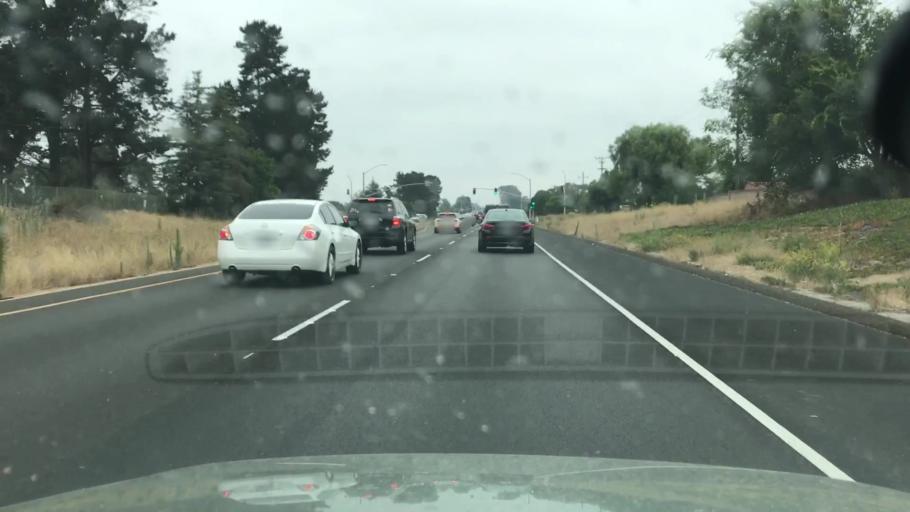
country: US
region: California
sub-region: Santa Barbara County
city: Orcutt
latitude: 34.9039
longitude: -120.4358
